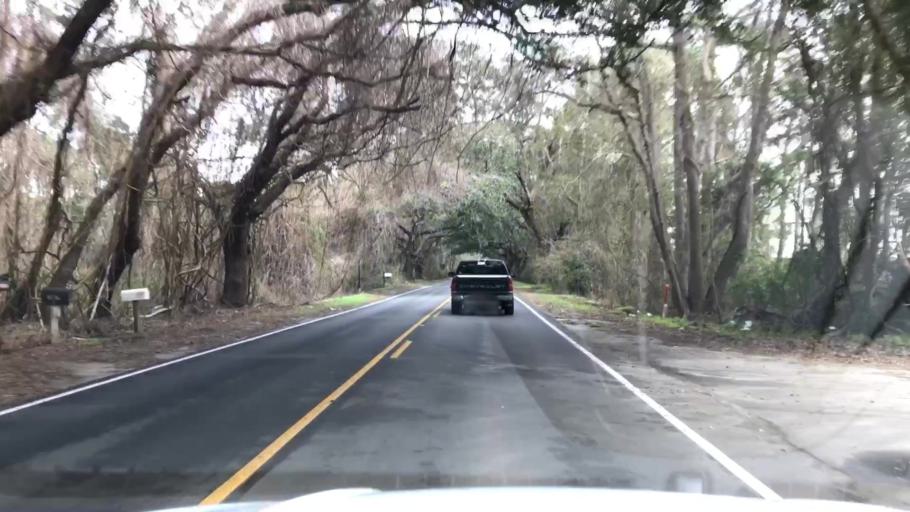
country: US
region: South Carolina
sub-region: Charleston County
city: Folly Beach
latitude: 32.6823
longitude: -80.0272
